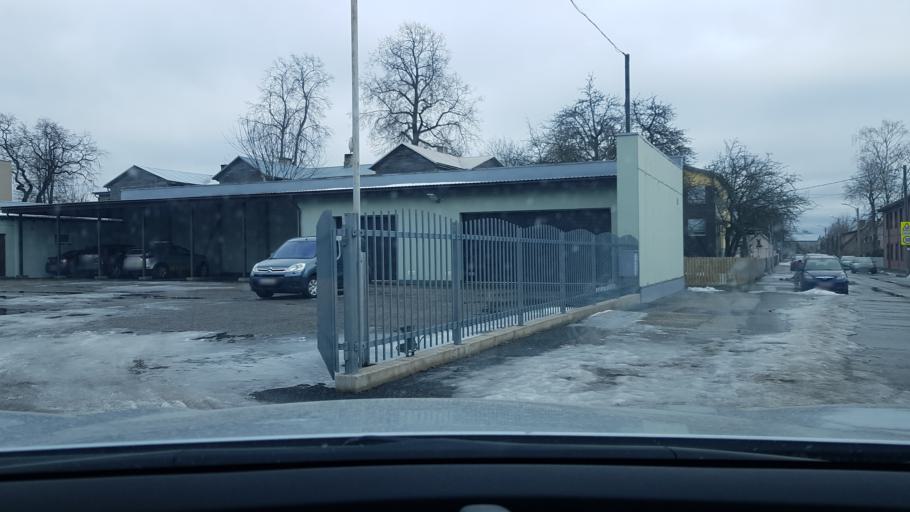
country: EE
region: Paernumaa
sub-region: Paernu linn
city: Parnu
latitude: 58.3799
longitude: 24.5109
